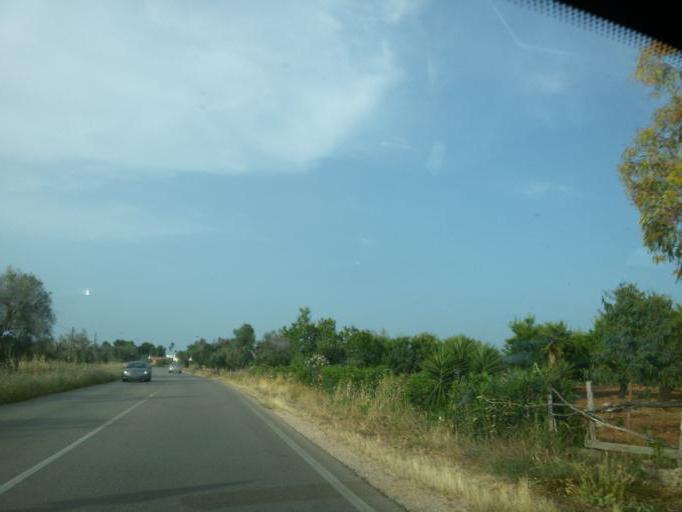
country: IT
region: Apulia
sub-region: Provincia di Brindisi
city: San Pietro Vernotico
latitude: 40.4819
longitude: 17.9849
